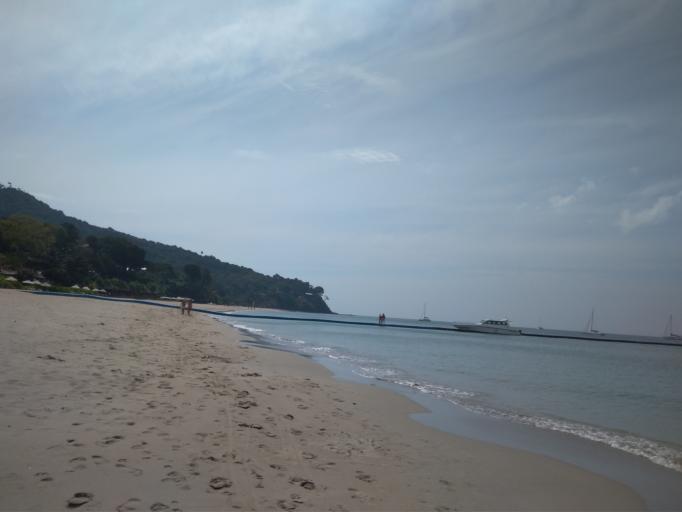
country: TH
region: Krabi
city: Ko Lanta
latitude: 7.4969
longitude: 99.0734
